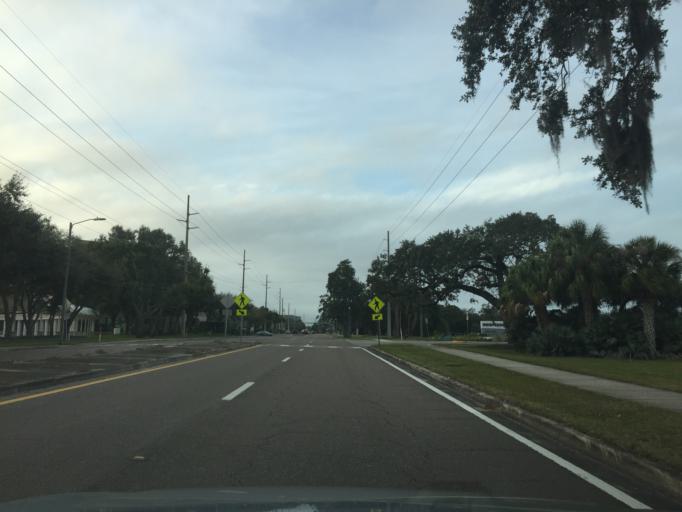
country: US
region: Florida
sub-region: Hillsborough County
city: Town 'n' Country
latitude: 27.9800
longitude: -82.5507
